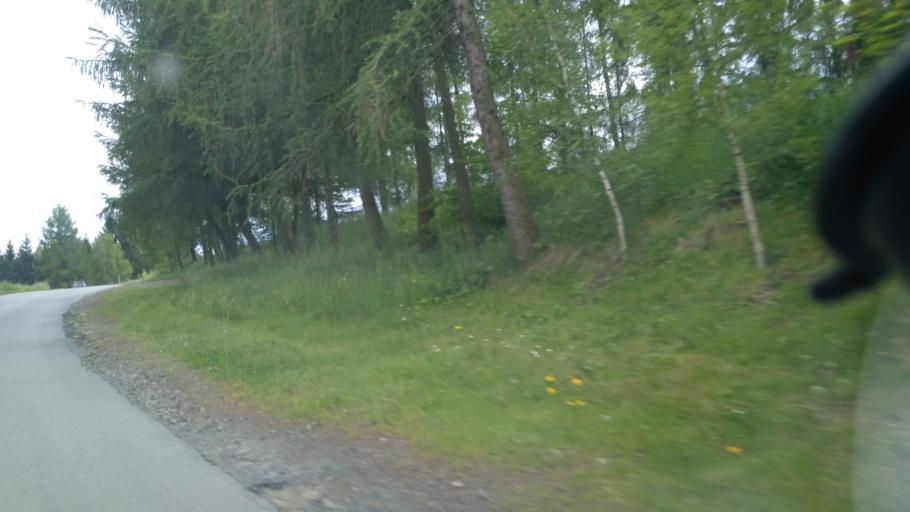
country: PL
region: Subcarpathian Voivodeship
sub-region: Powiat przemyski
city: Przedmiescie Dubieckie
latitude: 49.8284
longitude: 22.3267
